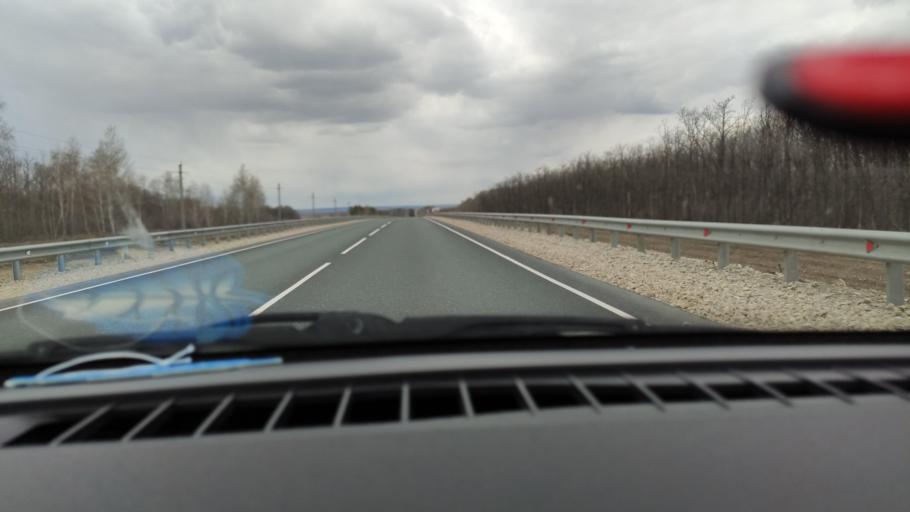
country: RU
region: Saratov
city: Shikhany
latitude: 52.1614
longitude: 47.1517
